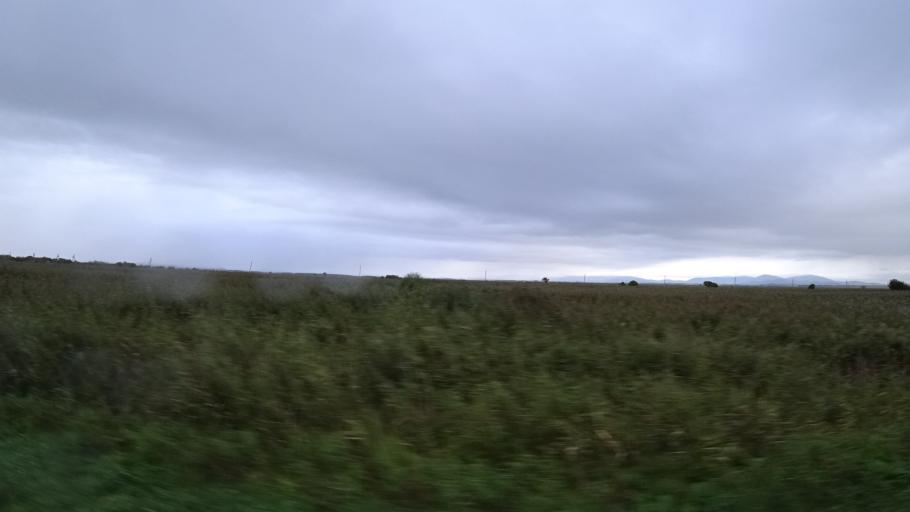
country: RU
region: Primorskiy
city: Chernigovka
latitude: 44.3911
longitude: 132.5291
